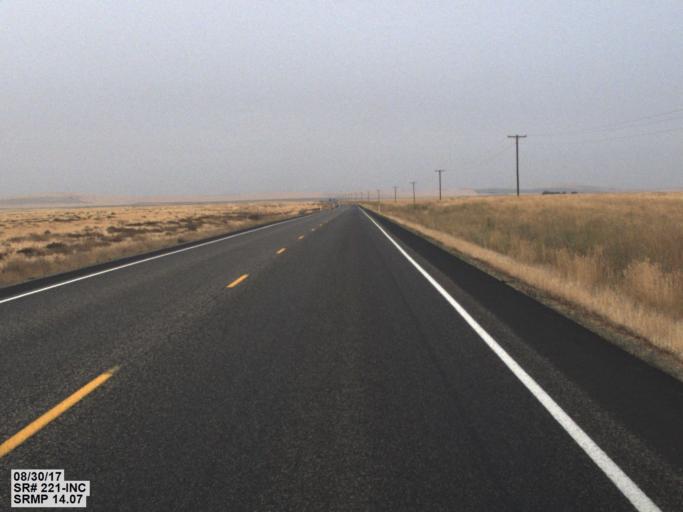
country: US
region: Washington
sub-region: Benton County
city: Benton City
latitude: 46.1389
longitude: -119.6012
